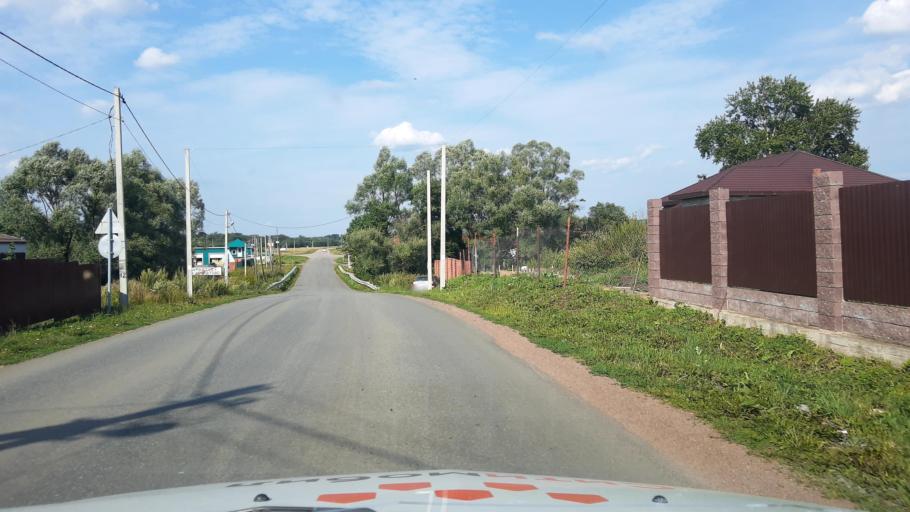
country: RU
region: Bashkortostan
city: Kabakovo
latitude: 54.6585
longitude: 56.1991
